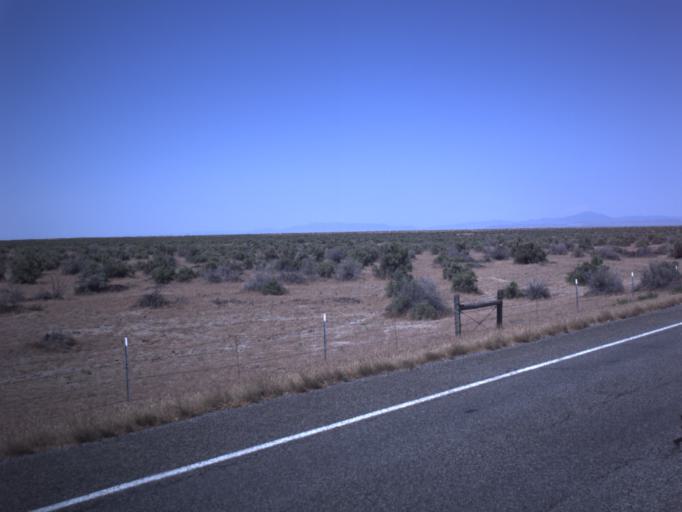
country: US
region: Utah
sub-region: Millard County
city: Delta
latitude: 39.4717
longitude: -112.4674
